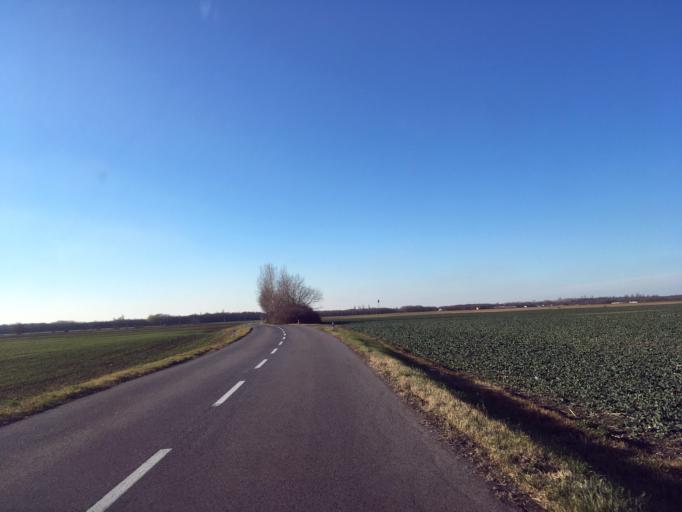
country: SK
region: Nitriansky
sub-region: Okres Komarno
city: Hurbanovo
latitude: 47.8956
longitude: 18.1817
